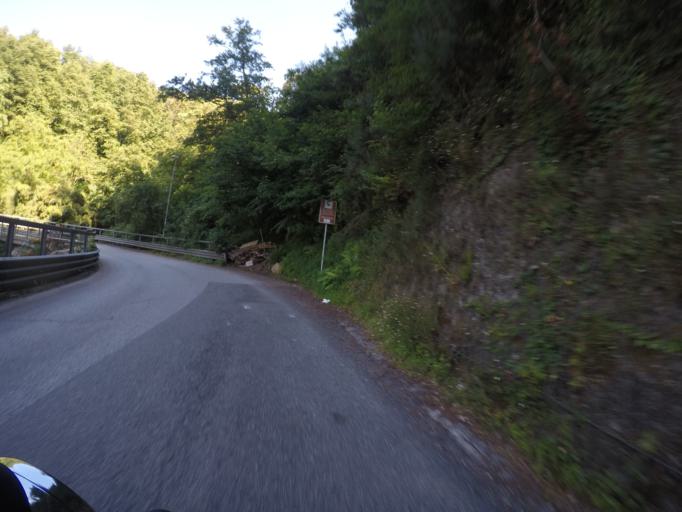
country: IT
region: Tuscany
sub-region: Provincia di Massa-Carrara
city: Montignoso
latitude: 44.0427
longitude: 10.1617
